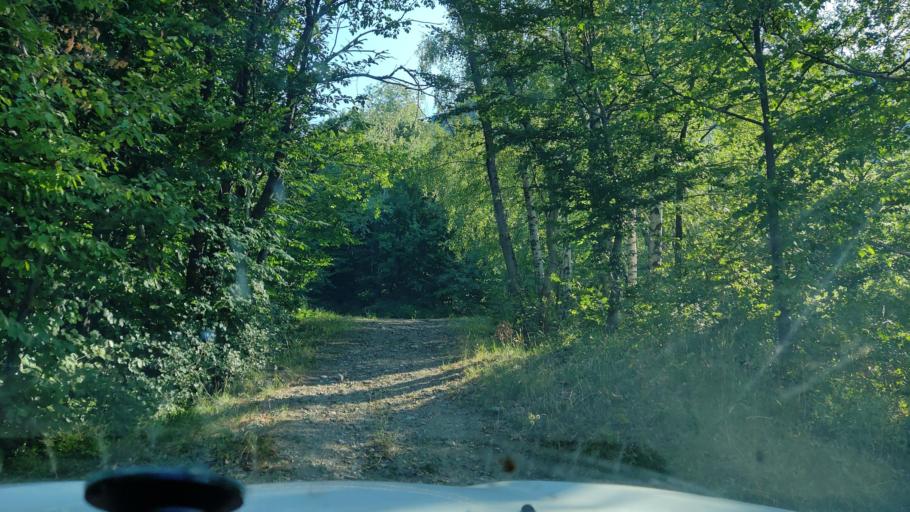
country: FR
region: Rhone-Alpes
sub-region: Departement de la Savoie
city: La Bathie
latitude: 45.5904
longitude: 6.4634
